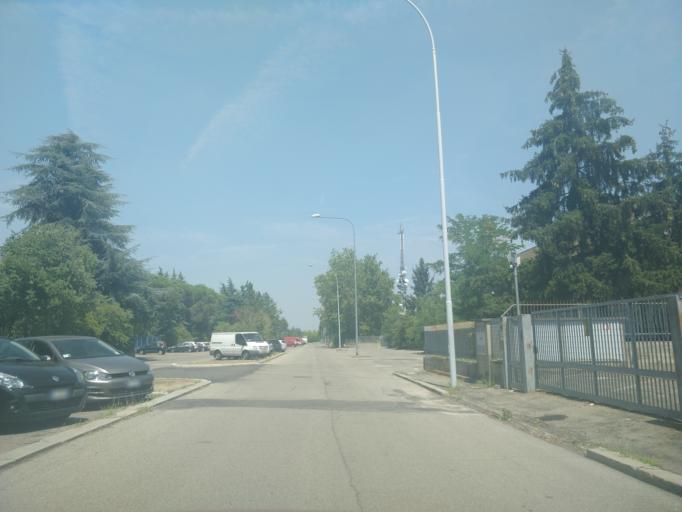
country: IT
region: Emilia-Romagna
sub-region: Provincia di Bologna
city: Progresso
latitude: 44.5612
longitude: 11.3712
